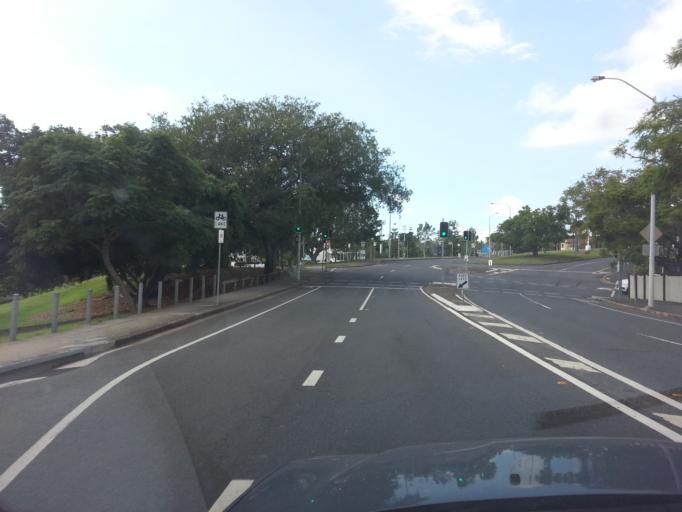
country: AU
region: Queensland
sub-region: Brisbane
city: Spring Hill
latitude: -27.4567
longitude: 153.0247
